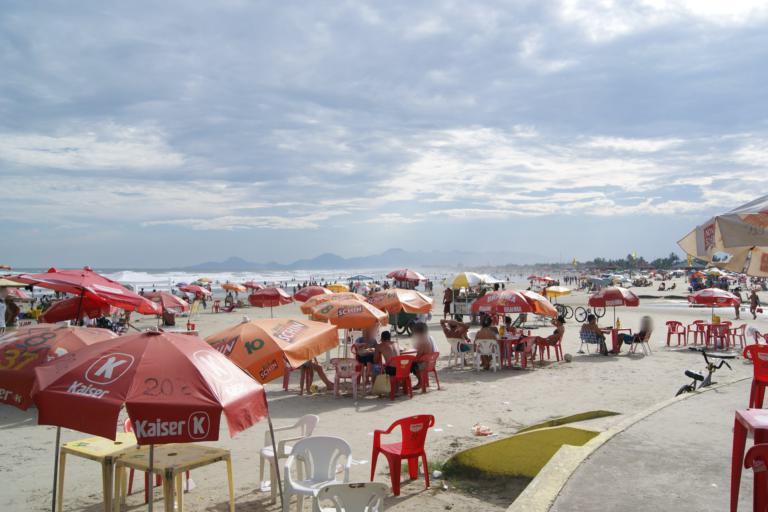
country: BR
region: Sao Paulo
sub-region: Itanhaem
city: Itanhaem
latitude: -24.2002
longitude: -46.8123
